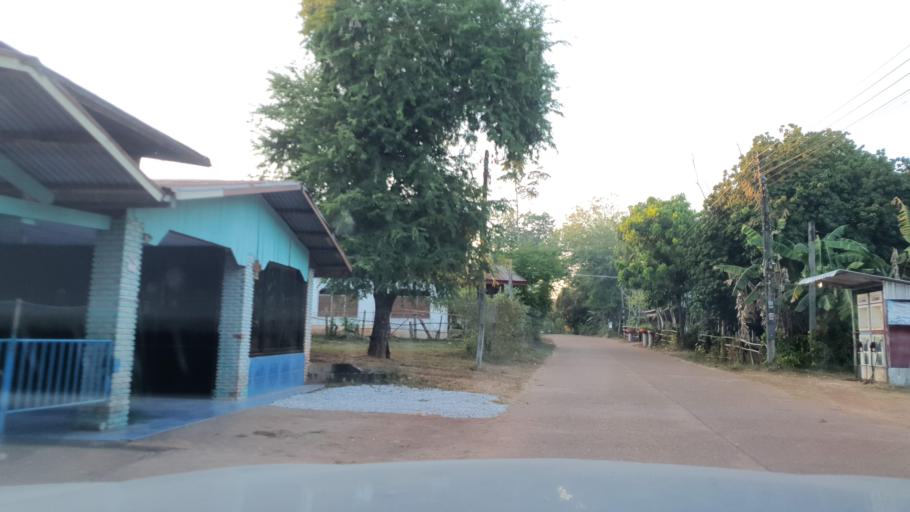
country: TH
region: Nakhon Phanom
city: Ban Phaeng
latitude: 17.8309
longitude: 104.2641
